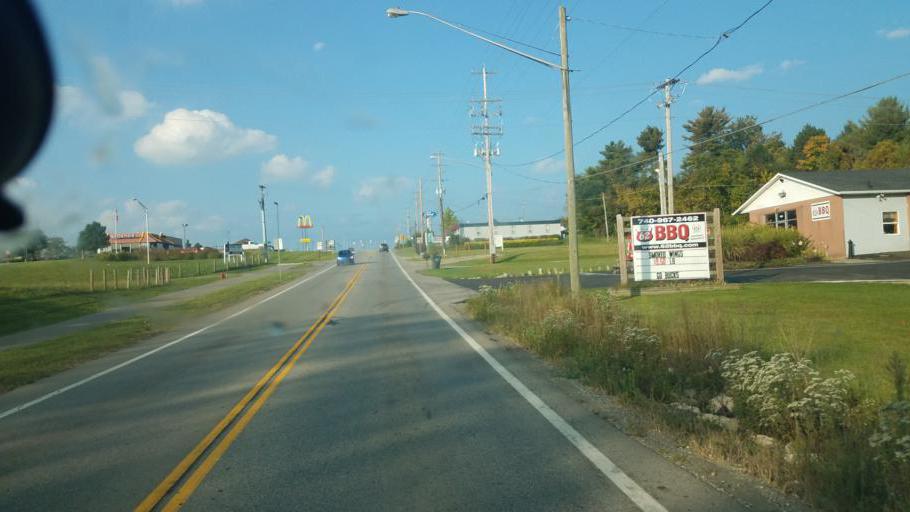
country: US
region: Ohio
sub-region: Licking County
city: Johnstown
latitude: 40.1483
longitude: -82.6994
